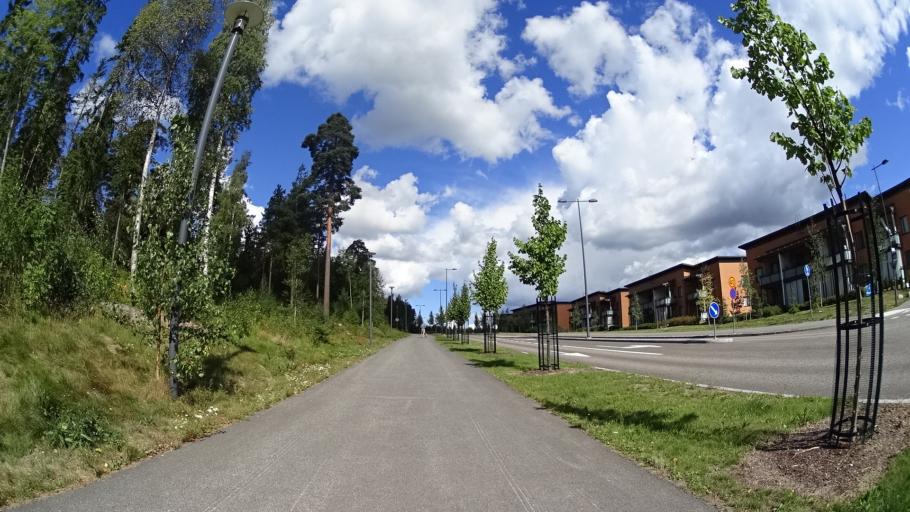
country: FI
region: Uusimaa
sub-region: Helsinki
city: Kilo
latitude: 60.2396
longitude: 24.8204
